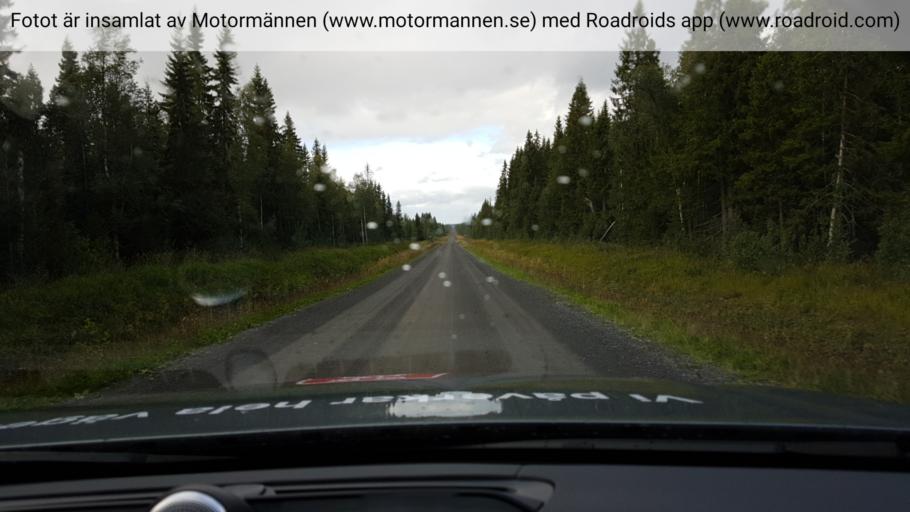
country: SE
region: Jaemtland
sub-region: OEstersunds Kommun
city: Lit
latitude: 63.6501
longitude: 14.9419
